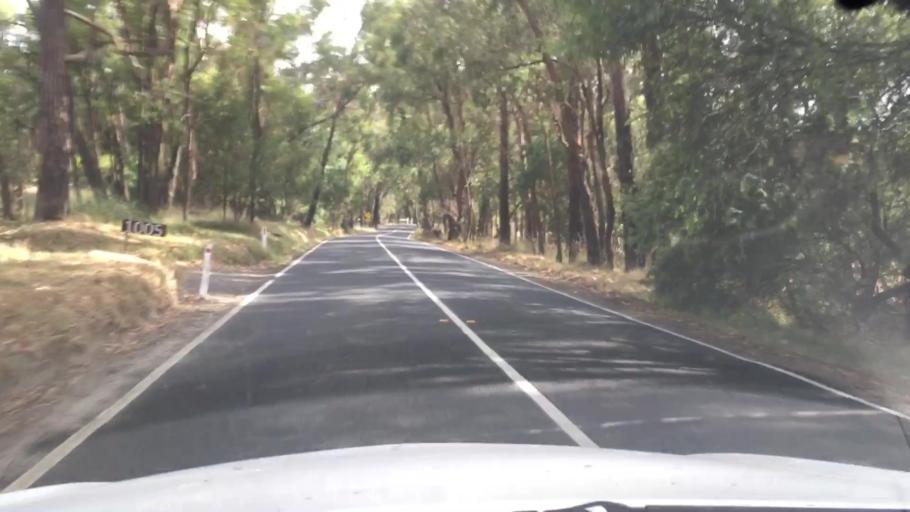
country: AU
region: Victoria
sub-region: Yarra Ranges
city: Macclesfield
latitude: -37.8400
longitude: 145.4869
